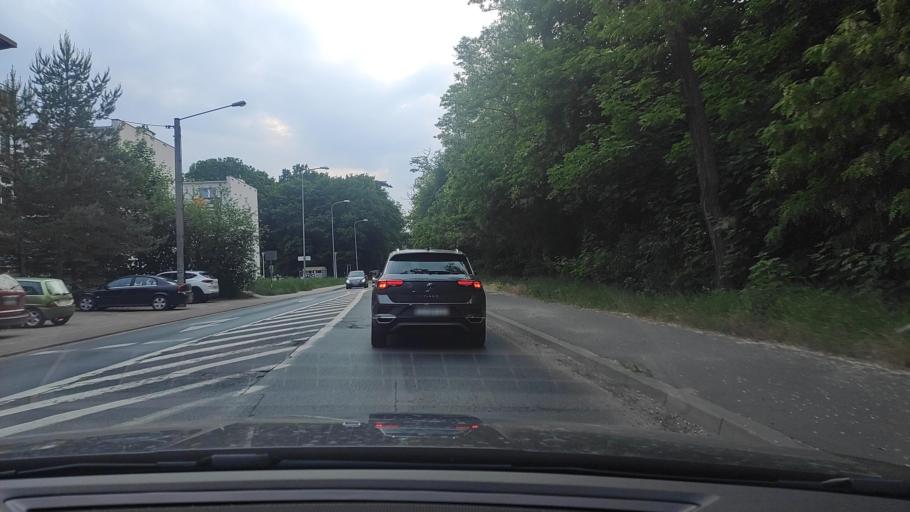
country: PL
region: Greater Poland Voivodeship
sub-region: Powiat poznanski
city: Czerwonak
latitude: 52.3918
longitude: 17.0064
